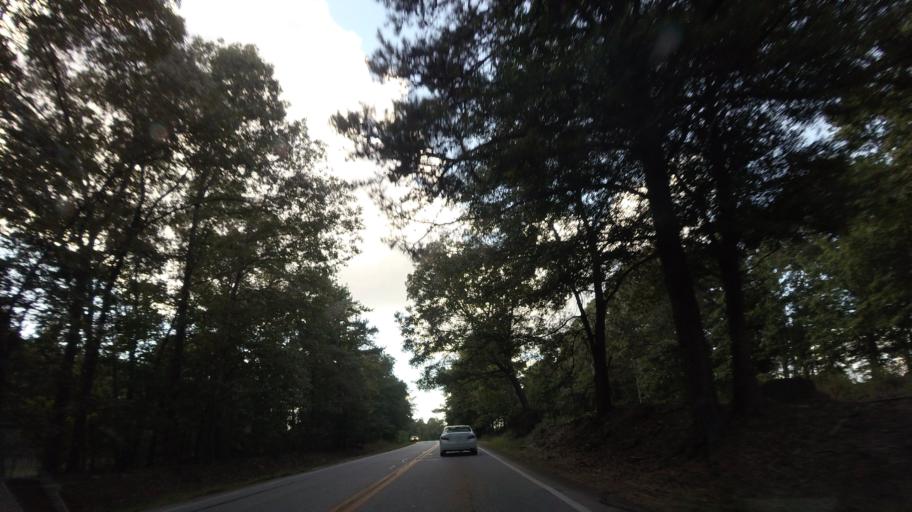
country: US
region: Georgia
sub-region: Lamar County
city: Barnesville
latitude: 33.0555
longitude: -84.0526
